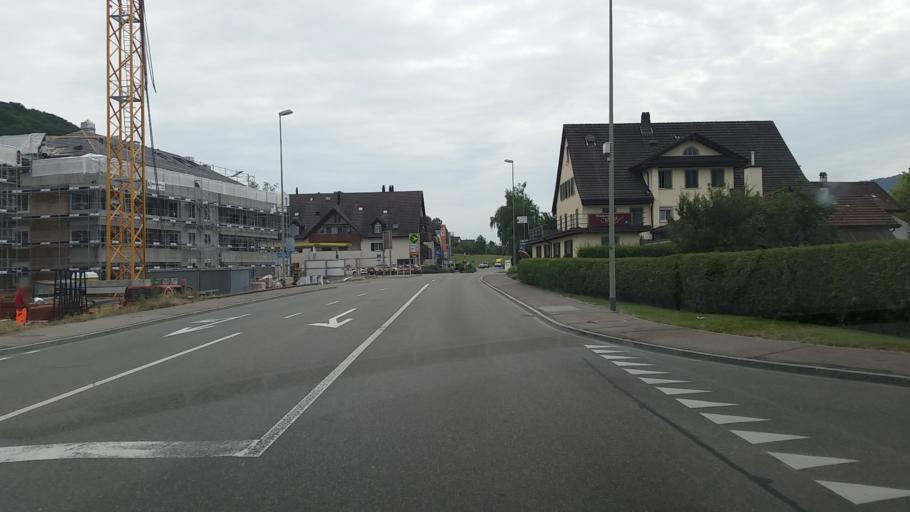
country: CH
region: Aargau
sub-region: Bezirk Baden
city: Unterehrendingen
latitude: 47.5078
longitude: 8.3788
